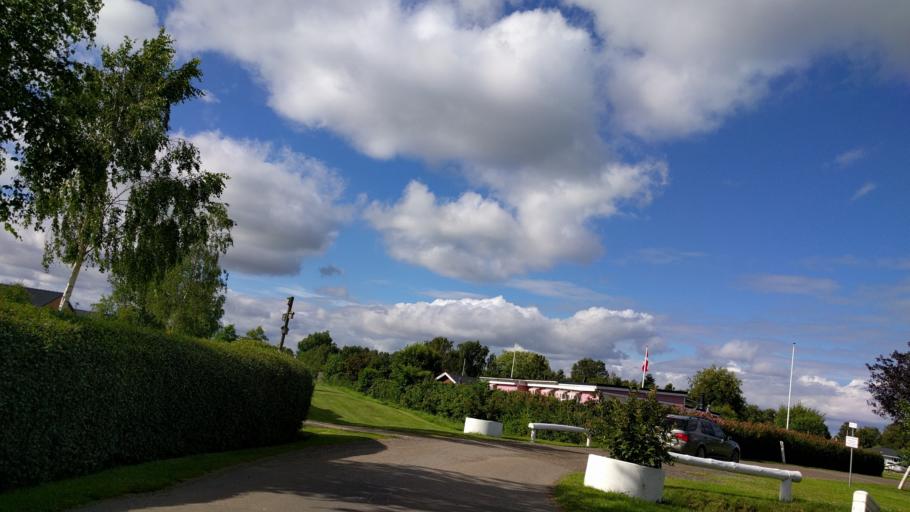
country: DK
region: Central Jutland
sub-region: Hedensted Kommune
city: Juelsminde
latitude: 55.7072
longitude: 10.0143
